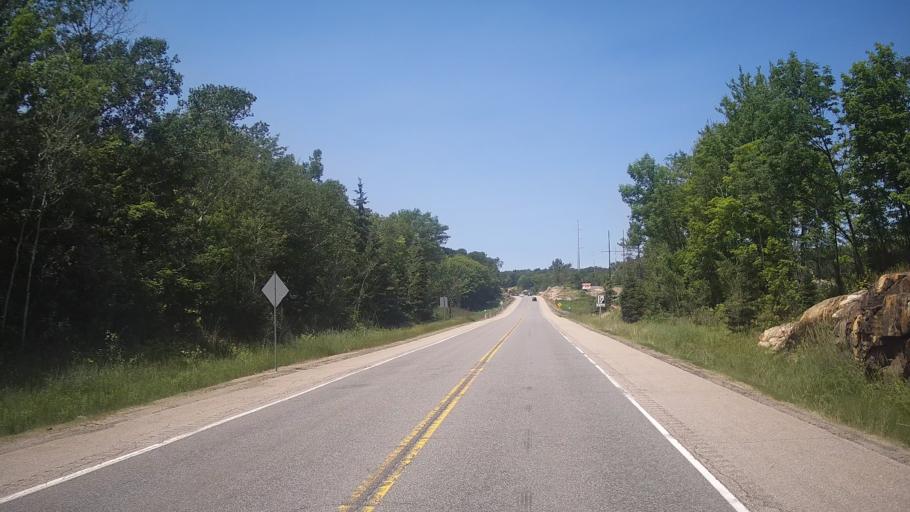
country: CA
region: Ontario
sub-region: Parry Sound District
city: Parry Sound
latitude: 45.5418
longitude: -80.2702
